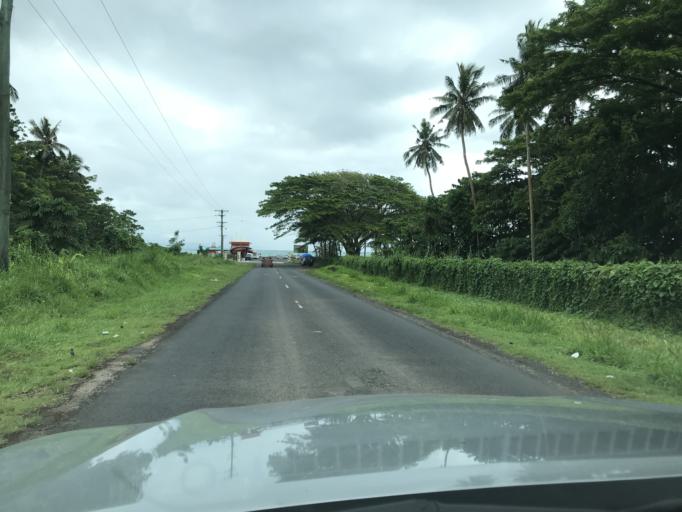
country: WS
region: Aiga-i-le-Tai
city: Mulifanua
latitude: -13.8310
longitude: -172.0337
